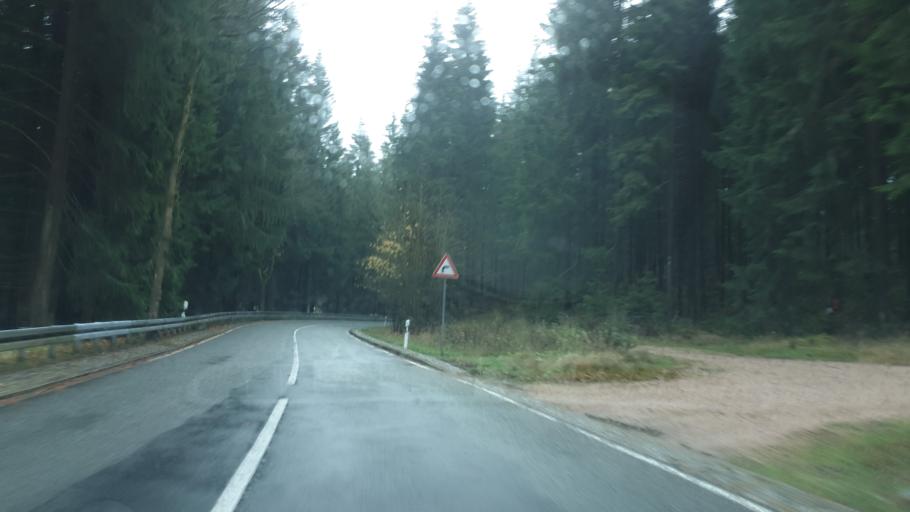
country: DE
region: Saxony
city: Muldenhammer
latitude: 50.4676
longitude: 12.5084
